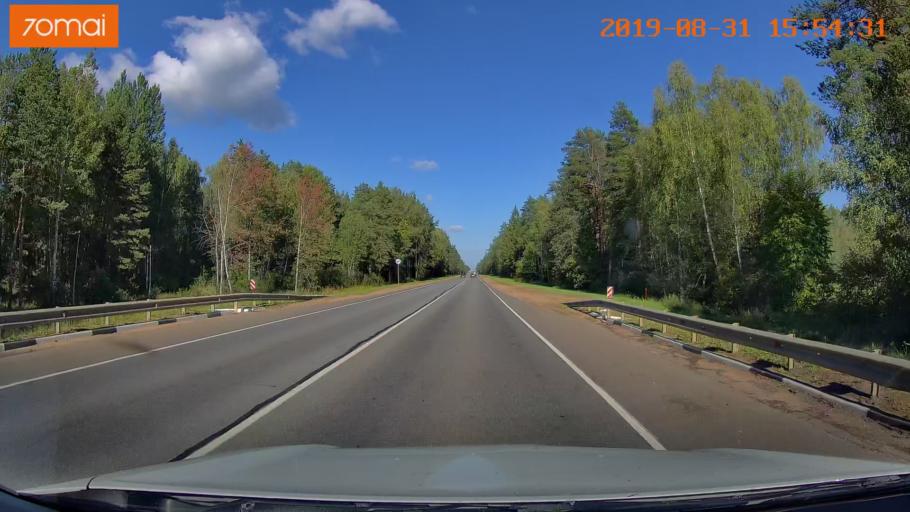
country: RU
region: Kaluga
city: Yukhnov
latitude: 54.7192
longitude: 35.1514
